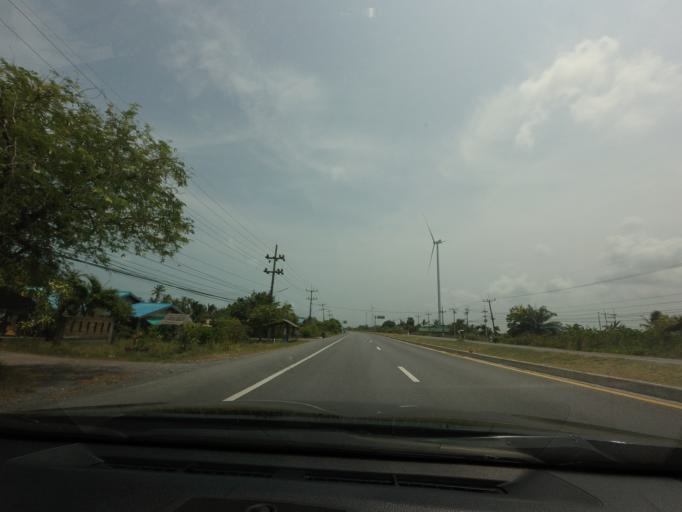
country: TH
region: Nakhon Si Thammarat
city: Hua Sai
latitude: 7.9716
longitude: 100.3274
